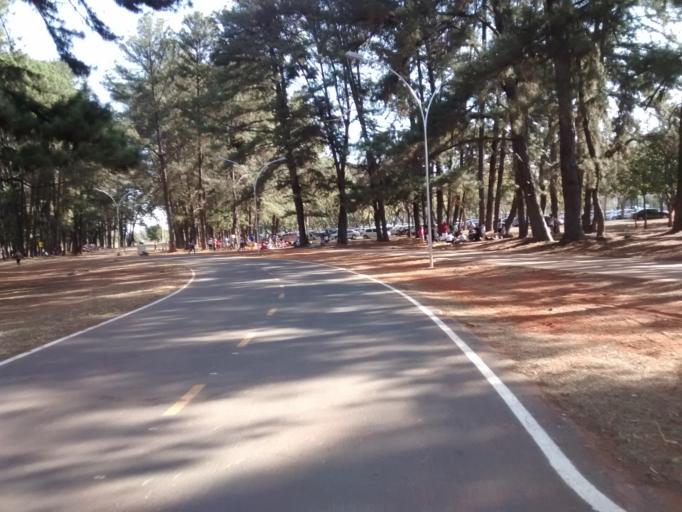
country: BR
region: Federal District
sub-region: Brasilia
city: Brasilia
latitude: -15.8035
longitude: -47.9179
